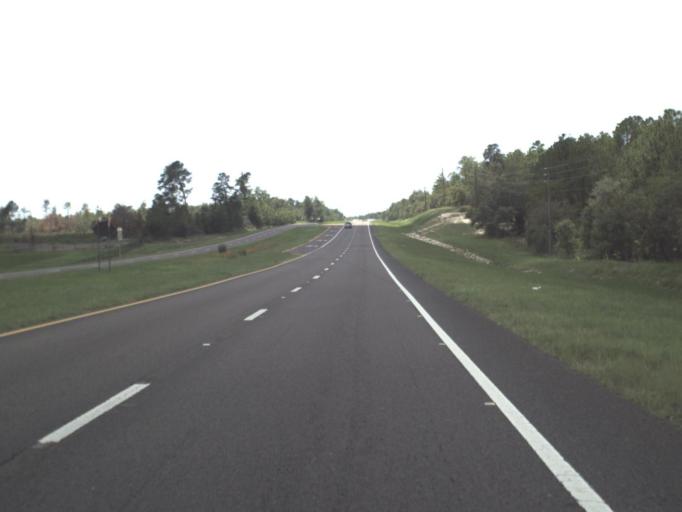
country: US
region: Florida
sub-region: Citrus County
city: Sugarmill Woods
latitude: 28.6904
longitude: -82.5016
